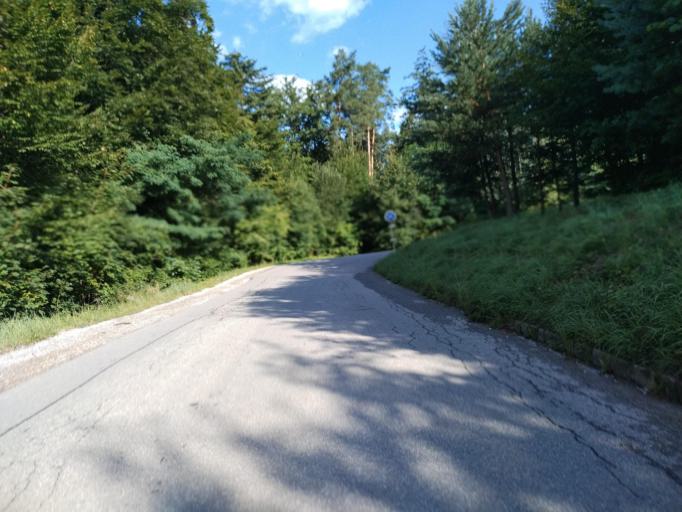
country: AT
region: Lower Austria
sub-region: Politischer Bezirk Wien-Umgebung
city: Pressbaum
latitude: 48.1838
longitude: 16.0786
